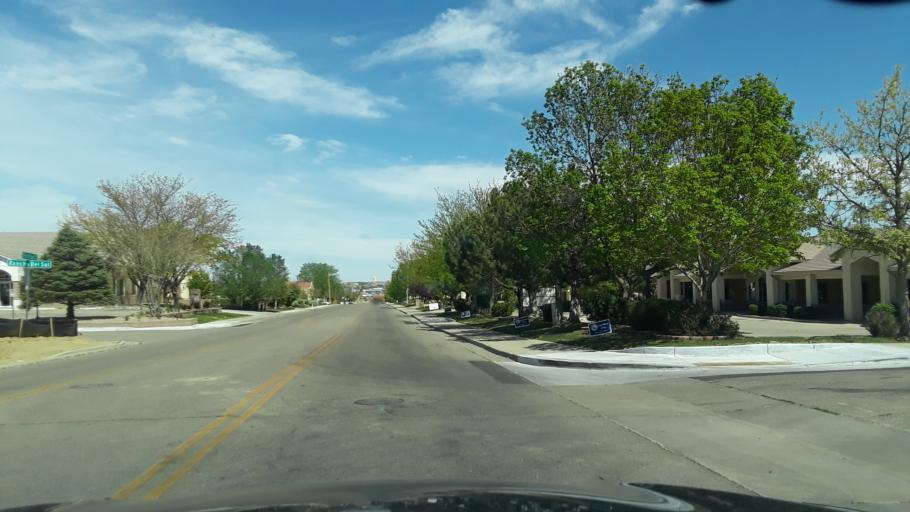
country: US
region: Colorado
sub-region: Pueblo County
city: Pueblo
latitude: 38.3125
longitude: -104.6252
